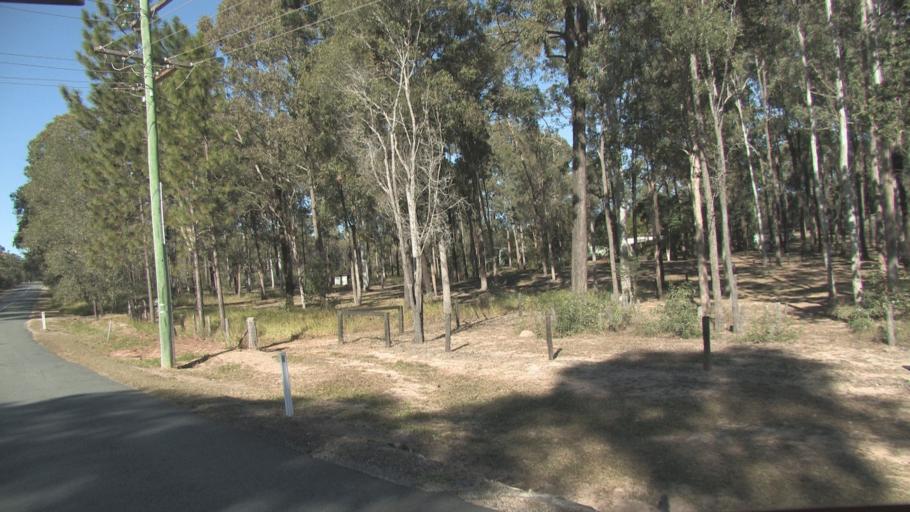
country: AU
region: Queensland
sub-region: Logan
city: Chambers Flat
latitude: -27.7937
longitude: 153.1397
